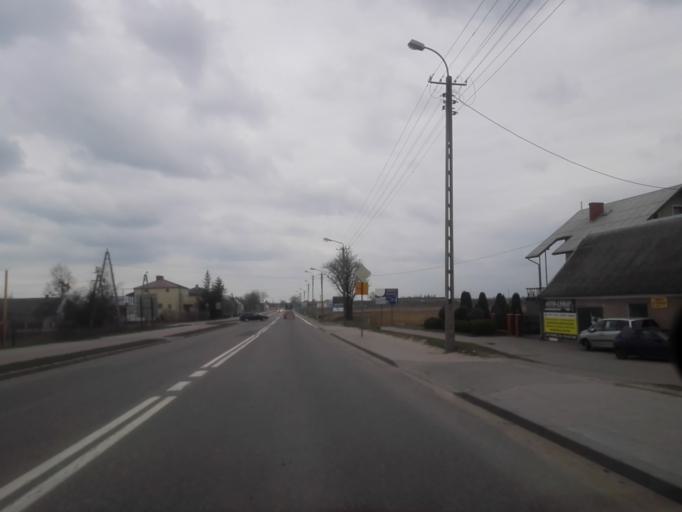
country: PL
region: Podlasie
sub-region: Powiat augustowski
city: Augustow
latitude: 53.8355
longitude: 22.9691
